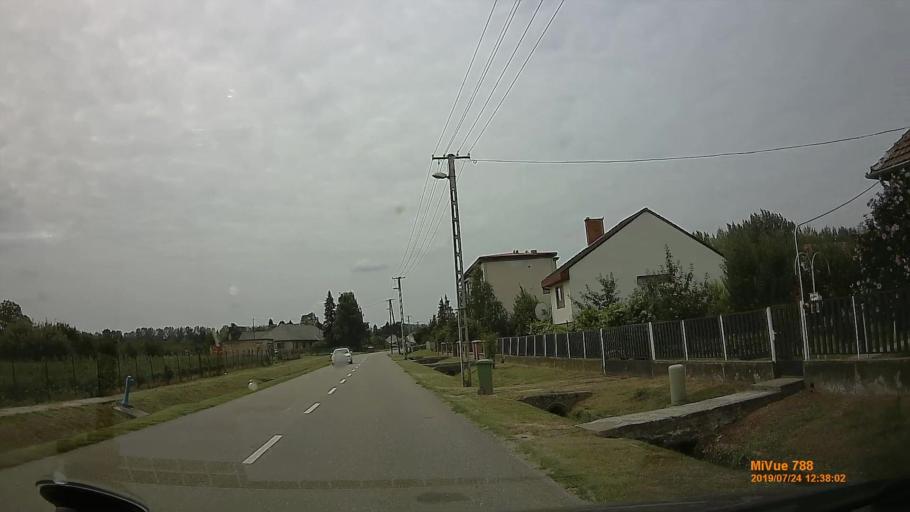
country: HU
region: Szabolcs-Szatmar-Bereg
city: Vasarosnameny
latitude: 48.1881
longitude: 22.3197
